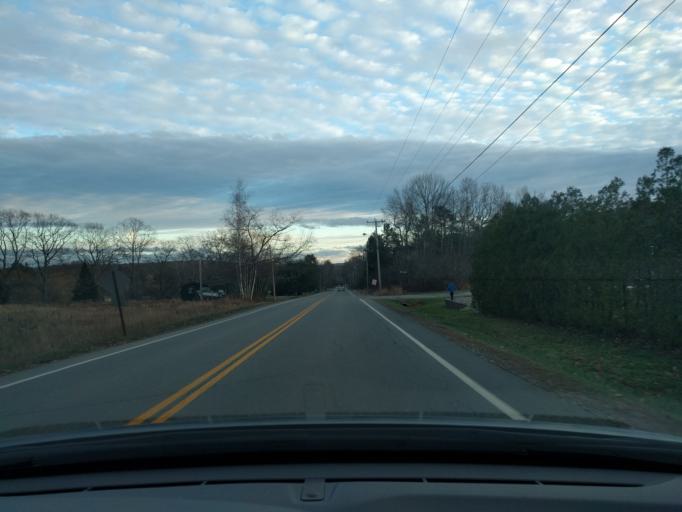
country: US
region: Maine
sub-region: Waldo County
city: Winterport
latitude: 44.6406
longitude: -68.8534
